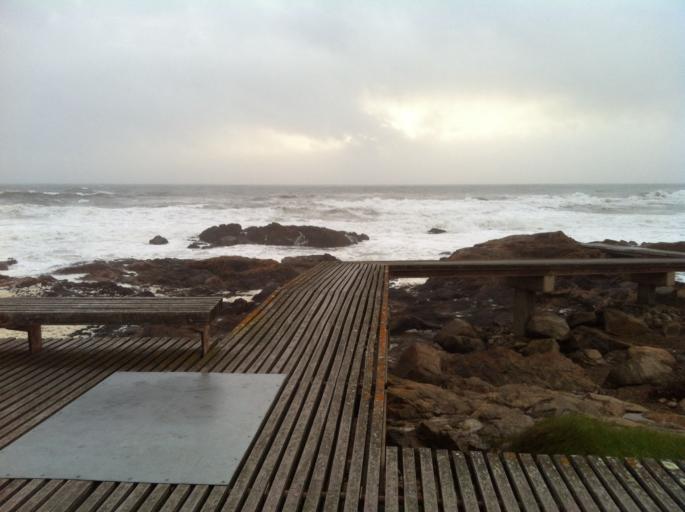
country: PT
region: Porto
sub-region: Matosinhos
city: Matosinhos
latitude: 41.1646
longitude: -8.6877
